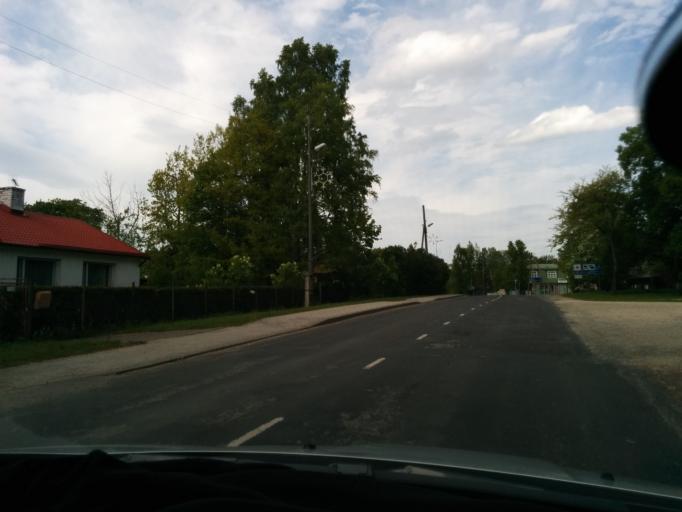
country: EE
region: Harju
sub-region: Loksa linn
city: Loksa
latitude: 59.5780
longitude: 25.7252
